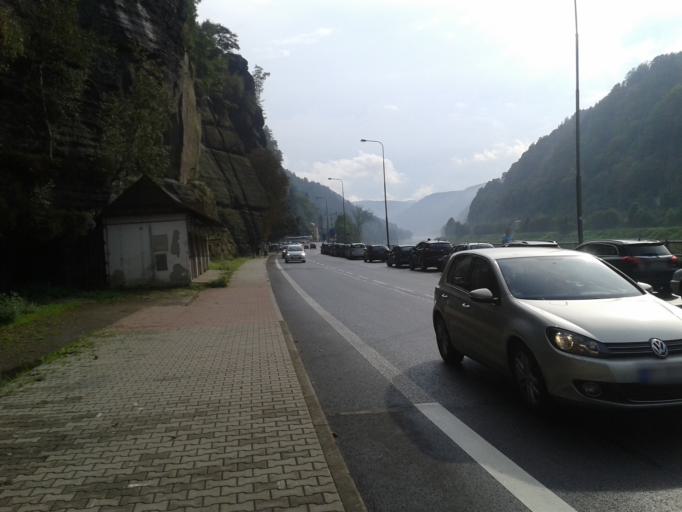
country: DE
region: Saxony
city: Bad Schandau
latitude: 50.8762
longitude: 14.2369
